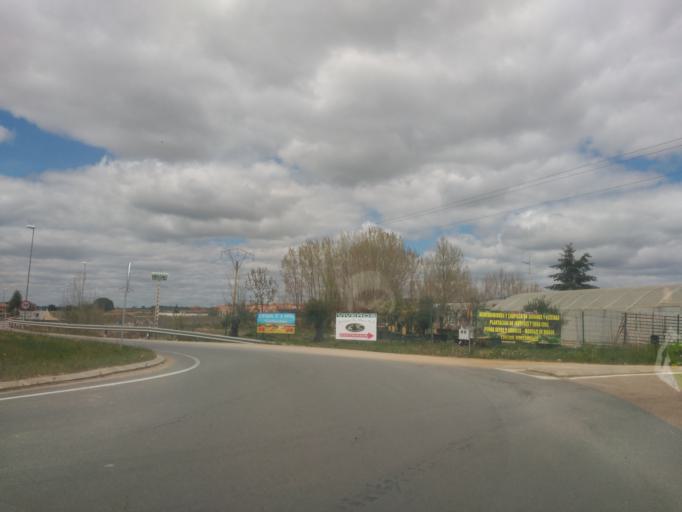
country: ES
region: Castille and Leon
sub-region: Provincia de Salamanca
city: Villamayor
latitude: 41.0091
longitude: -5.7070
